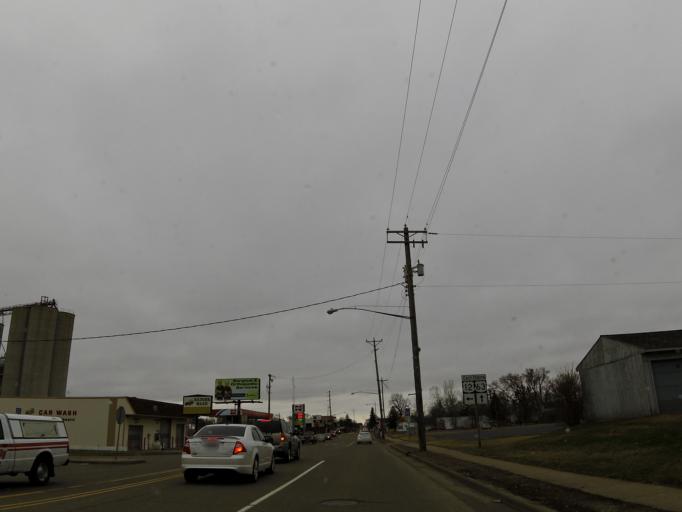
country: US
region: Wisconsin
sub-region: Saint Croix County
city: Baldwin
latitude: 44.9695
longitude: -92.3750
